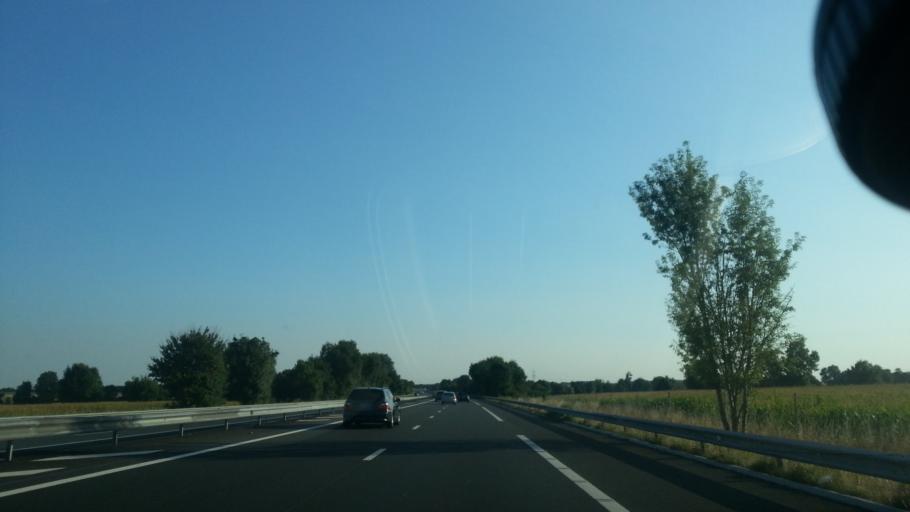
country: FR
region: Poitou-Charentes
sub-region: Departement des Deux-Sevres
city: Beauvoir-sur-Niort
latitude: 46.1523
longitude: -0.5190
